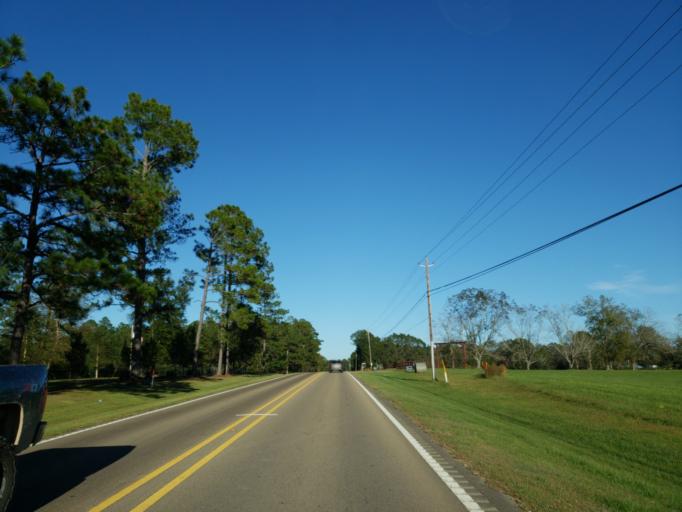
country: US
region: Mississippi
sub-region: Perry County
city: Richton
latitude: 31.3657
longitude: -88.8828
